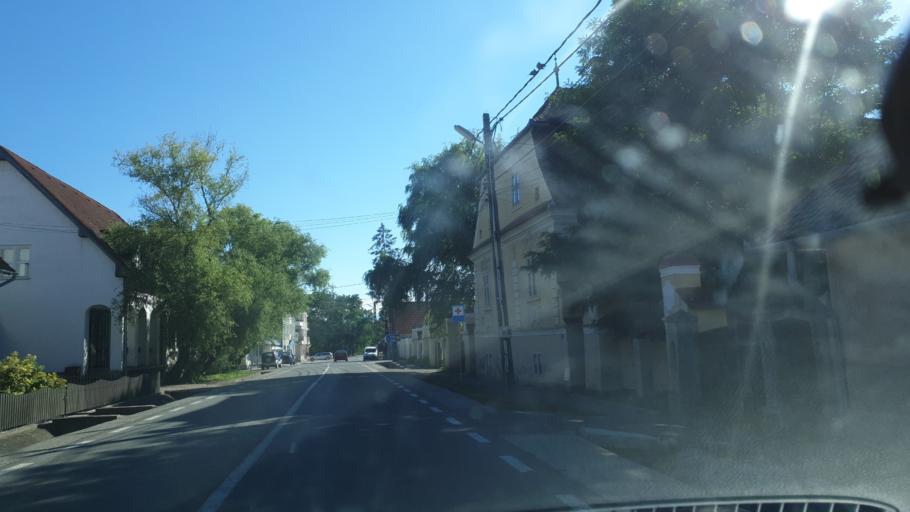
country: RO
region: Covasna
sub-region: Comuna Ilieni
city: Ilieni
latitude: 45.7960
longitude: 25.7715
